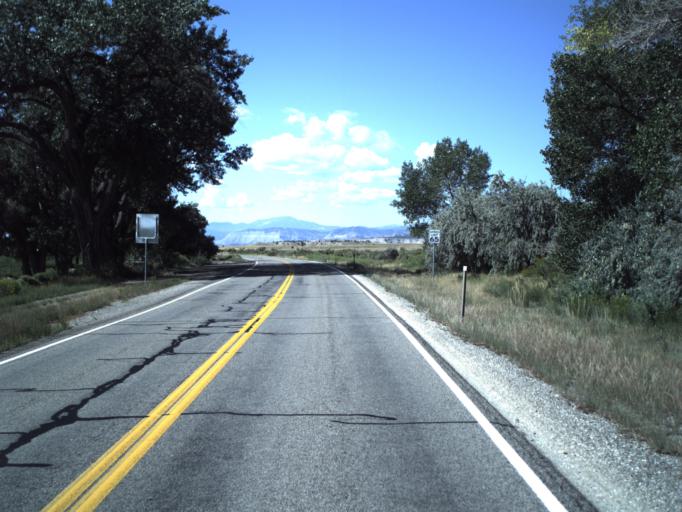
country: US
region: Utah
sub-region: Emery County
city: Ferron
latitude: 38.9201
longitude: -111.2607
